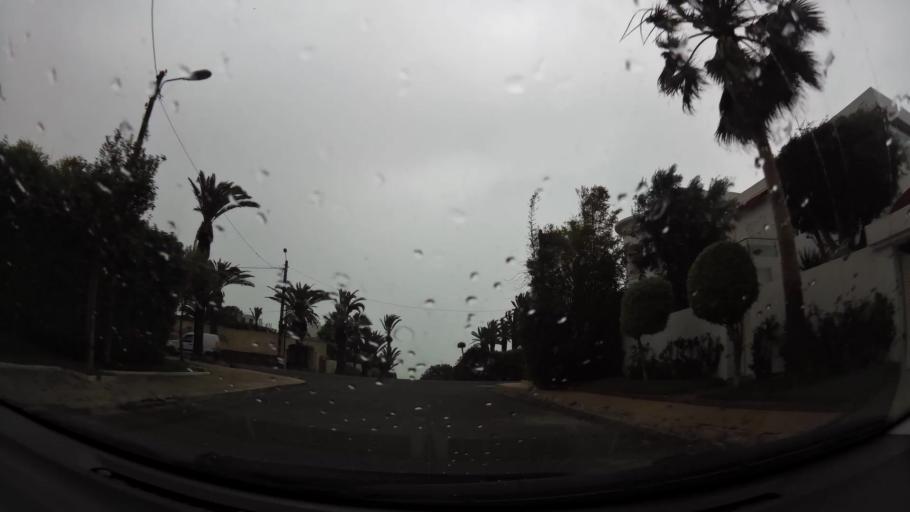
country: MA
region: Grand Casablanca
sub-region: Casablanca
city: Casablanca
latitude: 33.5895
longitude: -7.6778
